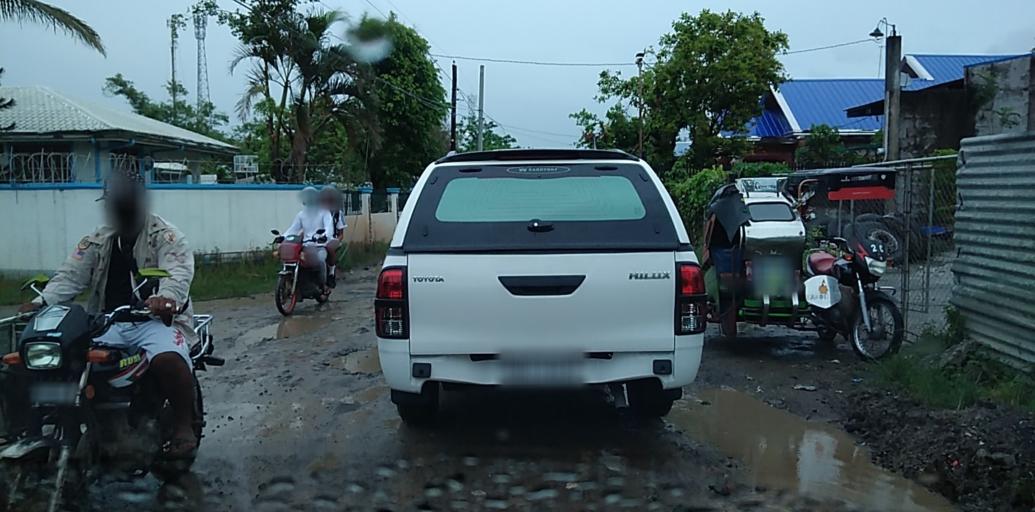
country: PH
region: Central Luzon
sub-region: Province of Pampanga
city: Batasan Bata
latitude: 15.1398
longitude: 120.9443
